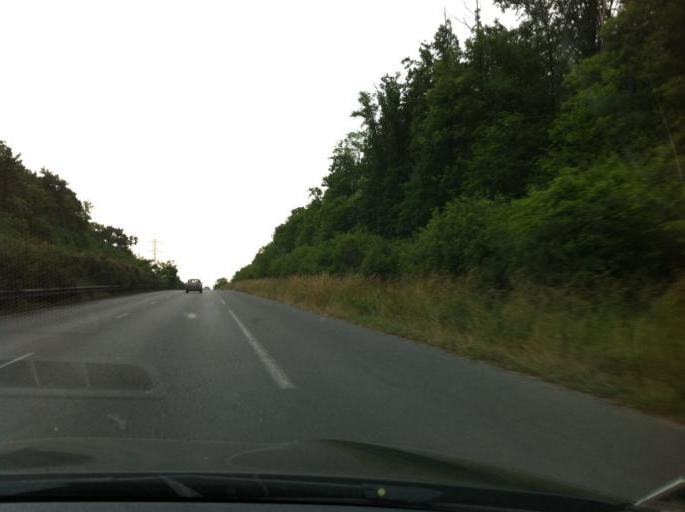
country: FR
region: Ile-de-France
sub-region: Departement de Seine-et-Marne
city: Voisenon
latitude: 48.5624
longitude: 2.6448
